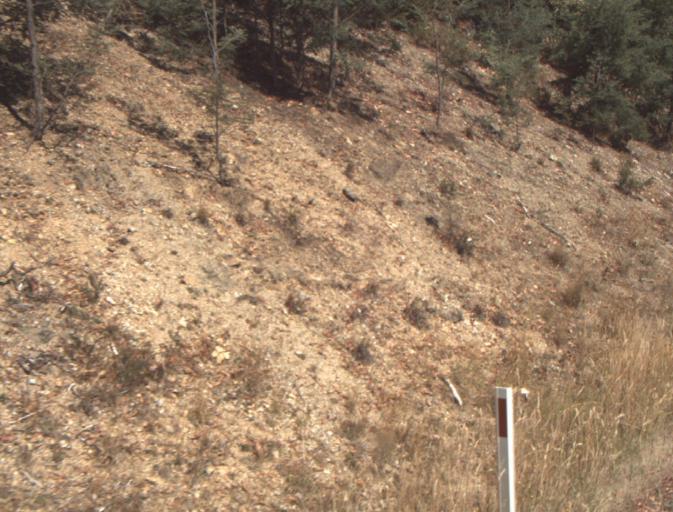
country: AU
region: Tasmania
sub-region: Dorset
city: Scottsdale
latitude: -41.3100
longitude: 147.3774
